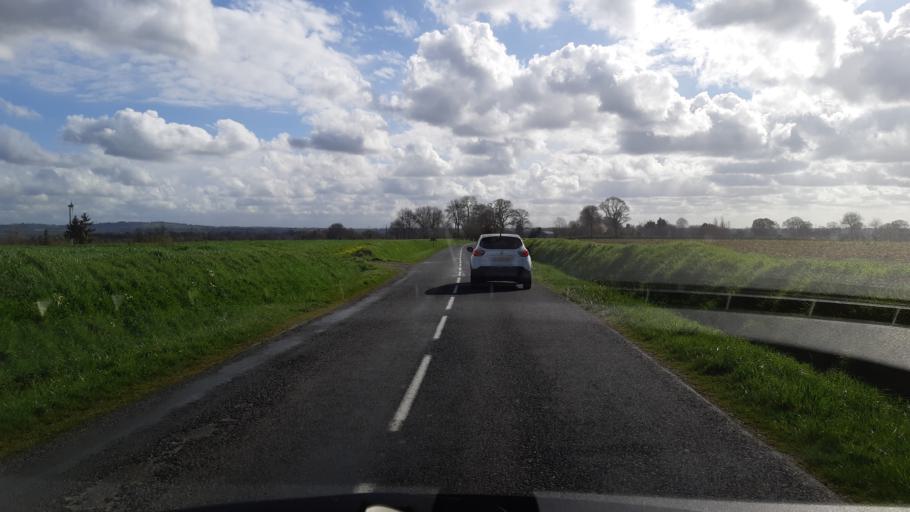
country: FR
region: Lower Normandy
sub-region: Departement de la Manche
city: Percy
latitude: 49.0182
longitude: -1.1624
